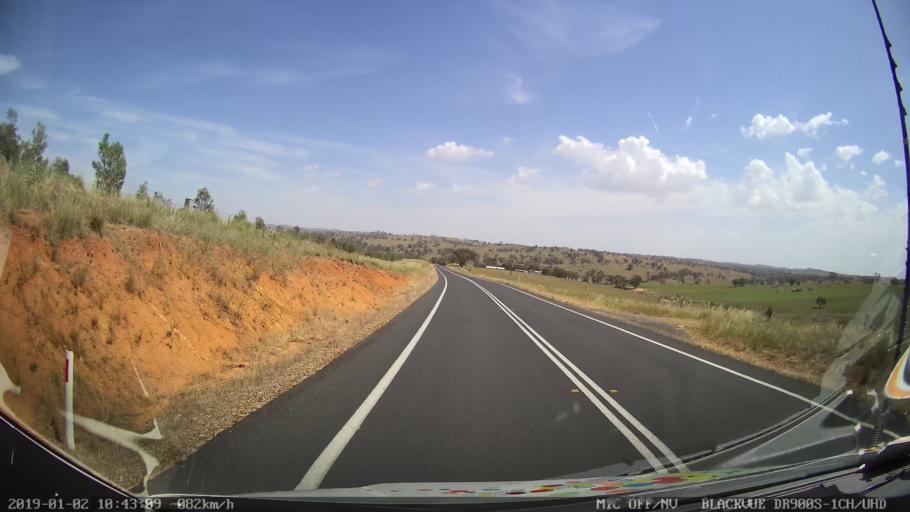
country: AU
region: New South Wales
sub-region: Cootamundra
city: Cootamundra
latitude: -34.7759
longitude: 148.3056
